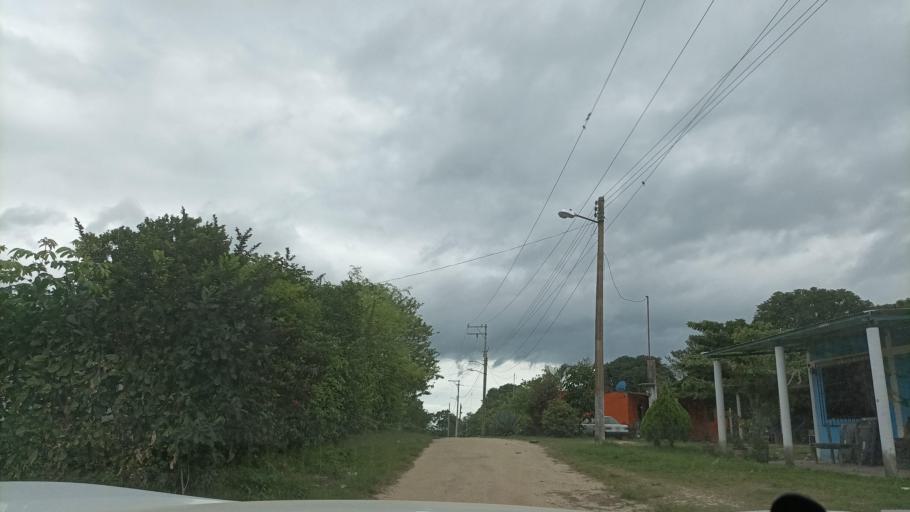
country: MX
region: Veracruz
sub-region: Cosoleacaque
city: Coacotla
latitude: 17.9441
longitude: -94.7067
